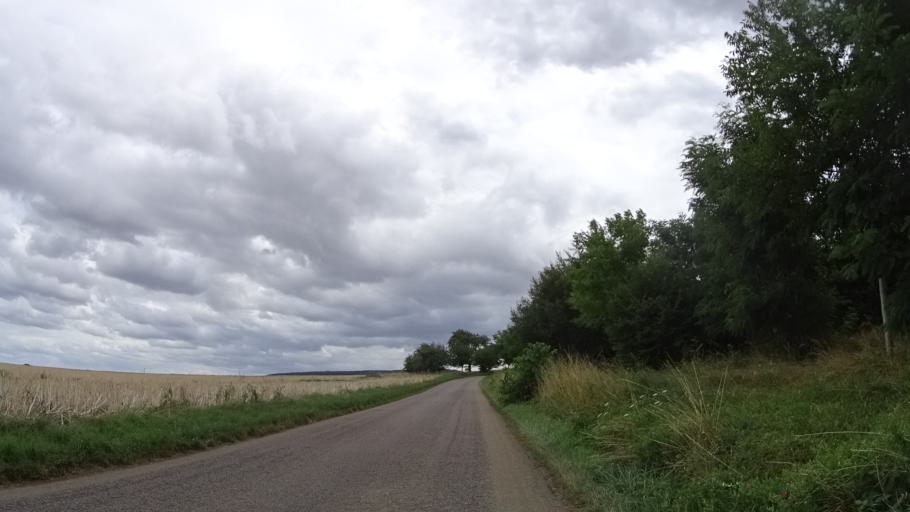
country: FR
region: Bourgogne
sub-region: Departement de l'Yonne
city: Cezy
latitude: 47.9655
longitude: 3.3572
